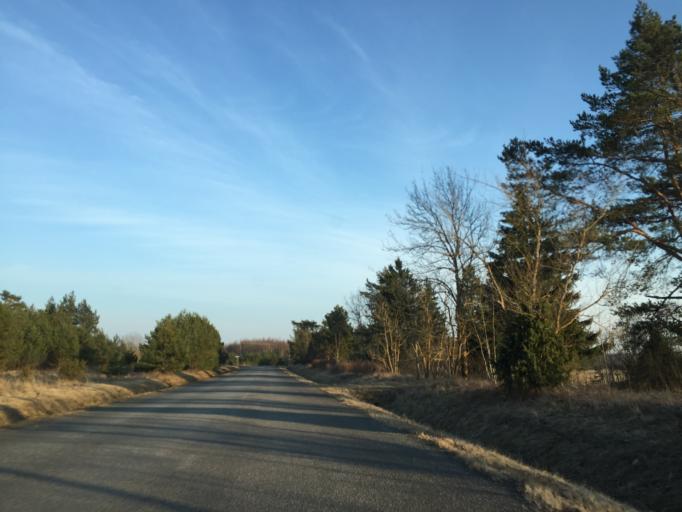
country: EE
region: Laeaene
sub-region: Lihula vald
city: Lihula
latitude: 58.4647
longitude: 23.7251
